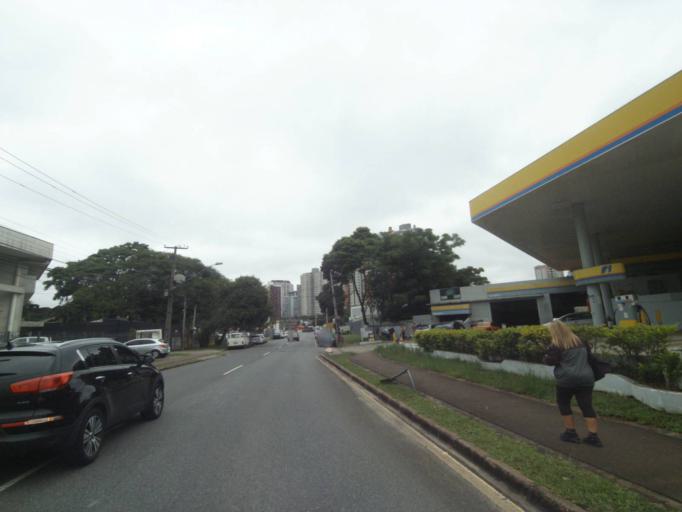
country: BR
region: Parana
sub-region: Curitiba
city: Curitiba
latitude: -25.4342
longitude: -49.3098
